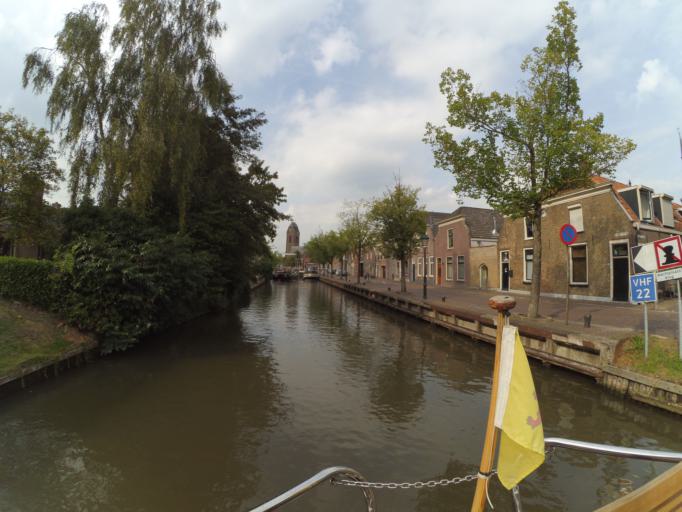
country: NL
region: Utrecht
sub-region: Gemeente IJsselstein
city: IJsselstein
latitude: 52.0329
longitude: 5.0369
